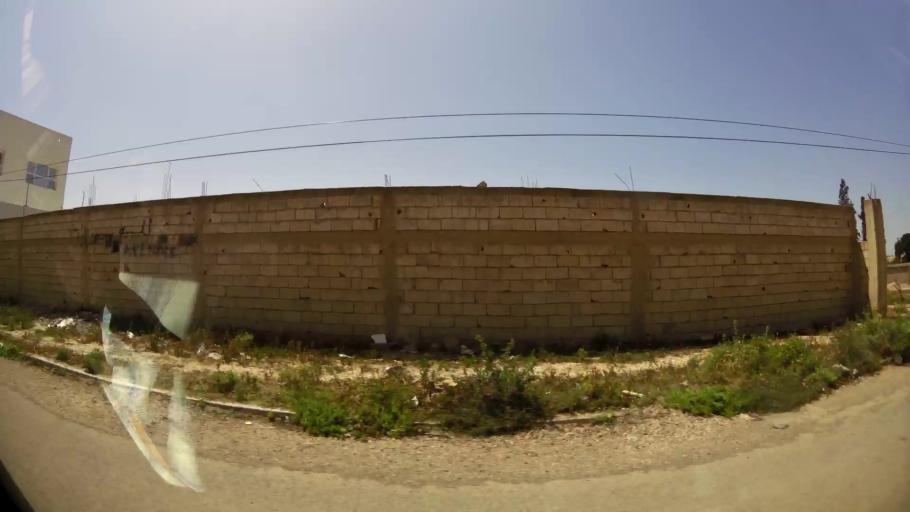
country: MA
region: Souss-Massa-Draa
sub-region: Inezgane-Ait Mellou
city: Inezgane
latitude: 30.3444
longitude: -9.5142
